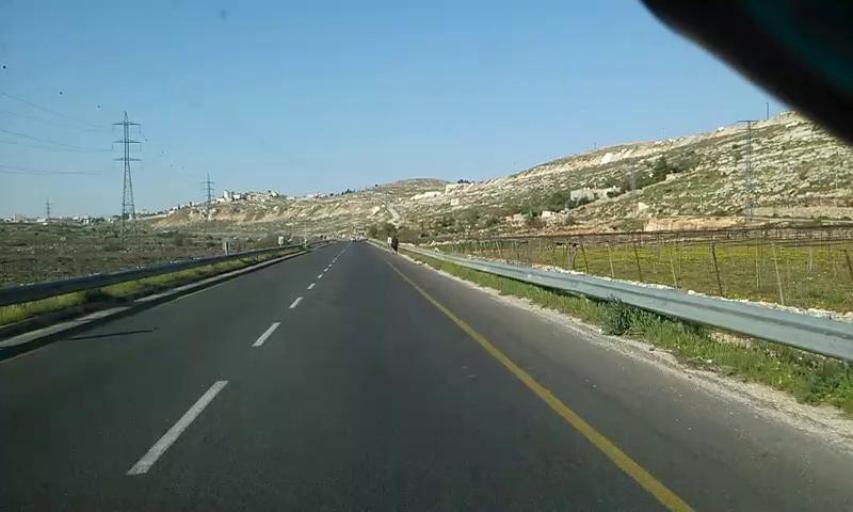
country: PS
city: Al Buq`ah
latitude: 31.5511
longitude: 35.1349
